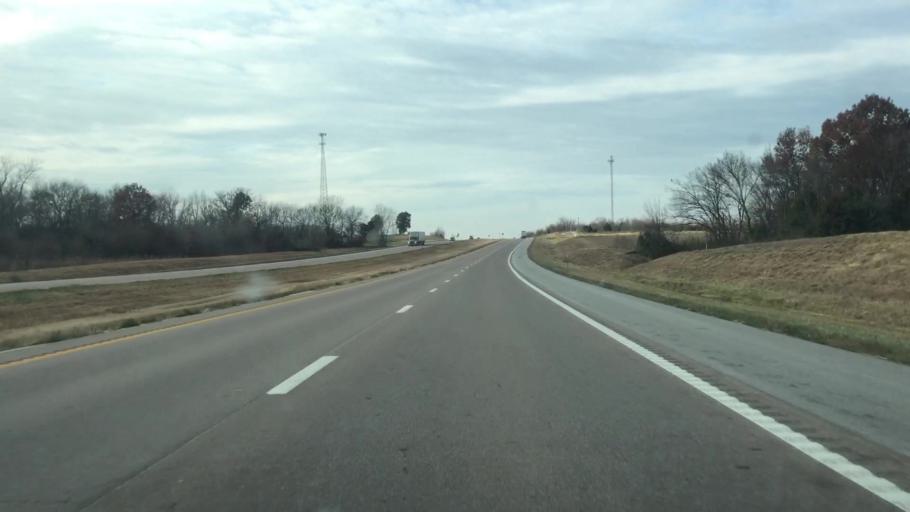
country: US
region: Missouri
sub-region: Cass County
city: Garden City
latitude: 38.4765
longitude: -94.0227
